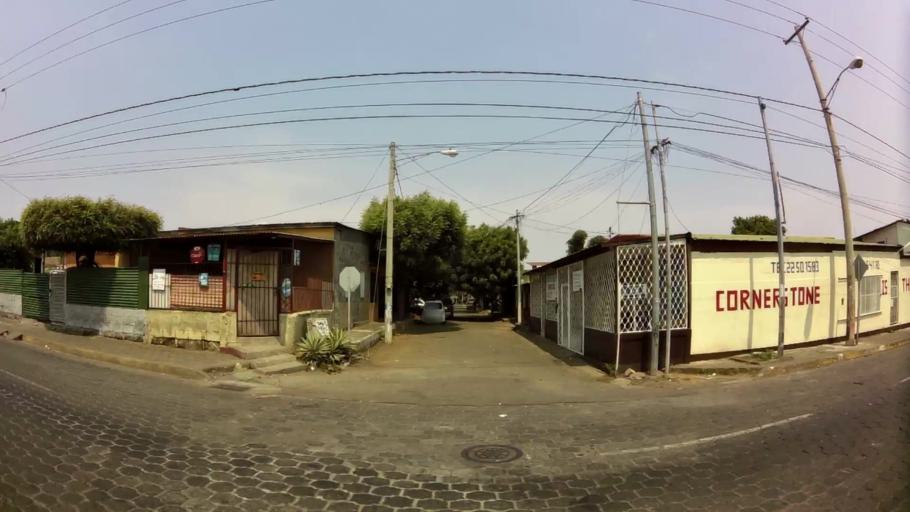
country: NI
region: Managua
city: Ciudad Sandino
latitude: 12.1523
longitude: -86.2972
